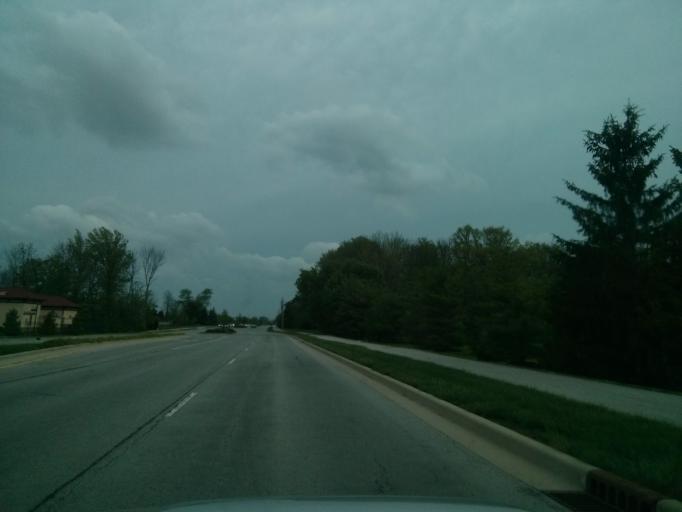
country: US
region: Indiana
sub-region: Boone County
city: Zionsville
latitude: 39.9643
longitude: -86.2027
